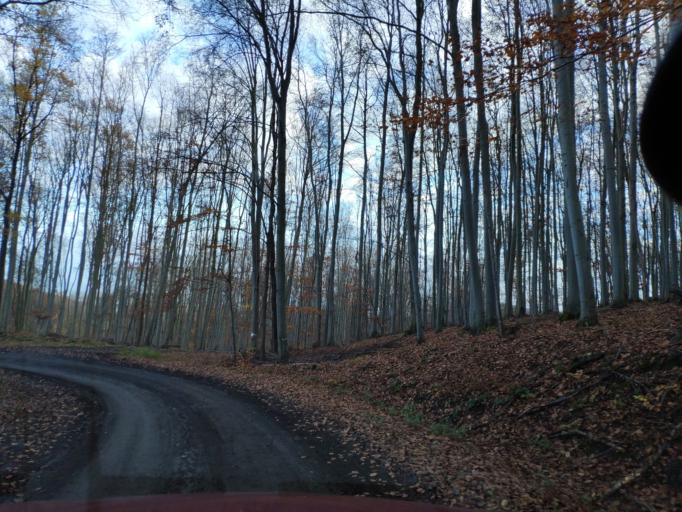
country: SK
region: Kosicky
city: Secovce
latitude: 48.5781
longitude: 21.4800
